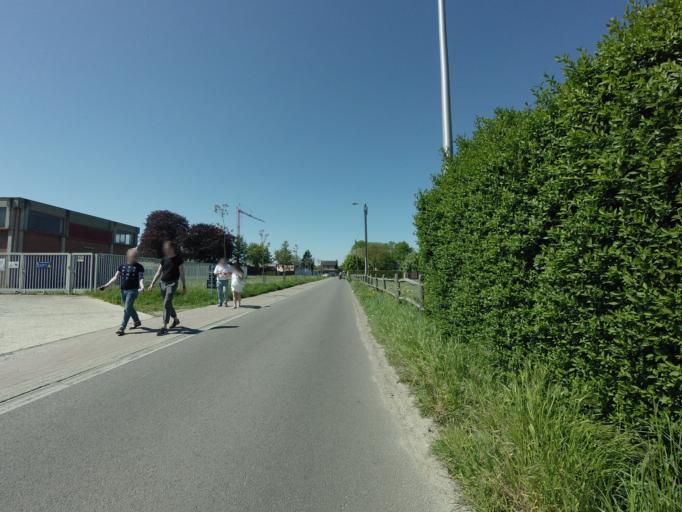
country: BE
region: Flanders
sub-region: Provincie Antwerpen
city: Essen
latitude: 51.4691
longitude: 4.4487
